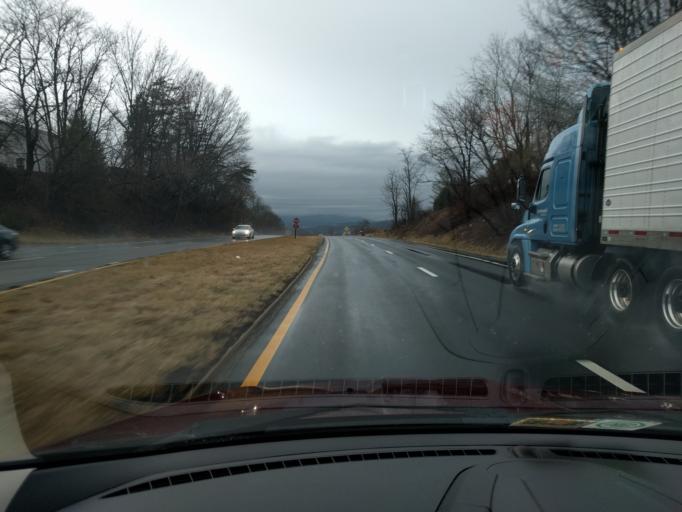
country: US
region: Virginia
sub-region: Giles County
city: Pembroke
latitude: 37.3216
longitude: -80.5990
